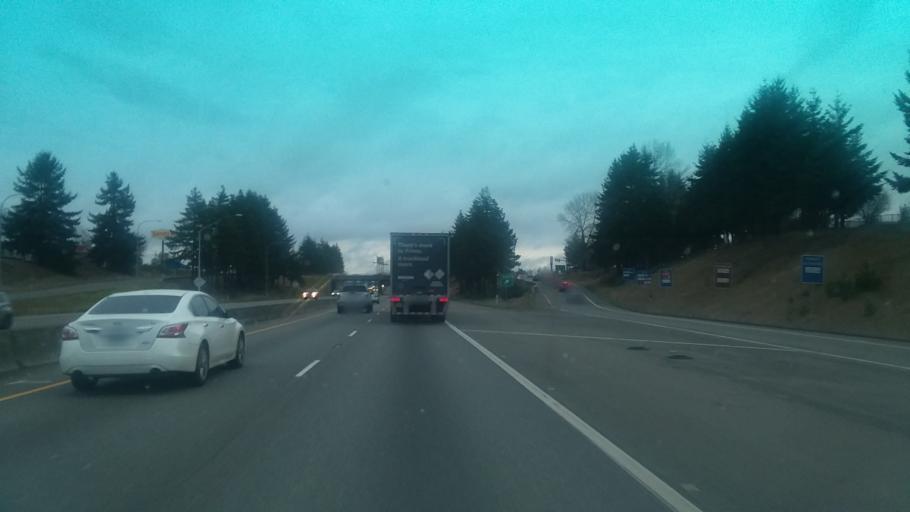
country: US
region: Washington
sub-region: Pierce County
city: Parkland
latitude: 47.1582
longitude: -122.4379
